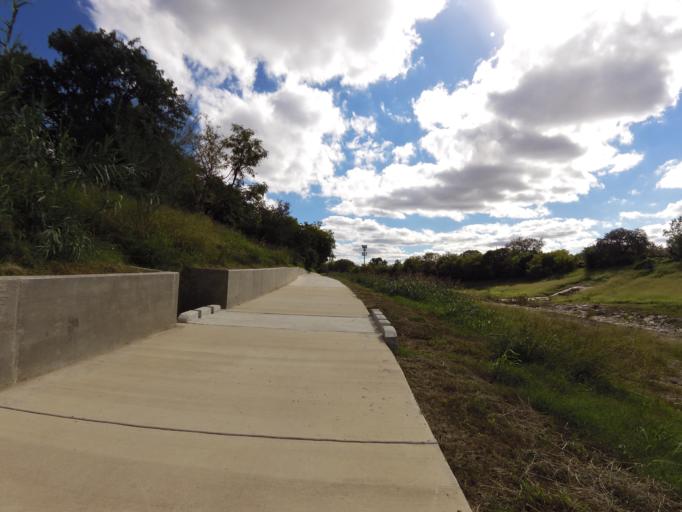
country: US
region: Texas
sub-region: Bexar County
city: San Antonio
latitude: 29.3948
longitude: -98.5031
